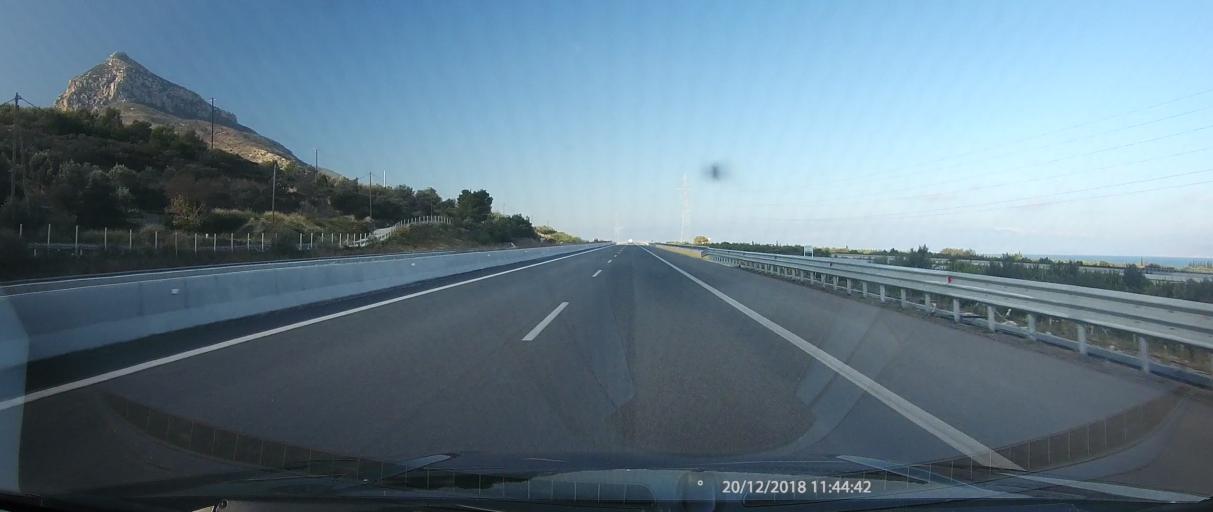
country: GR
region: Peloponnese
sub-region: Nomos Korinthias
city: Xylokastro
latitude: 38.0821
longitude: 22.5927
